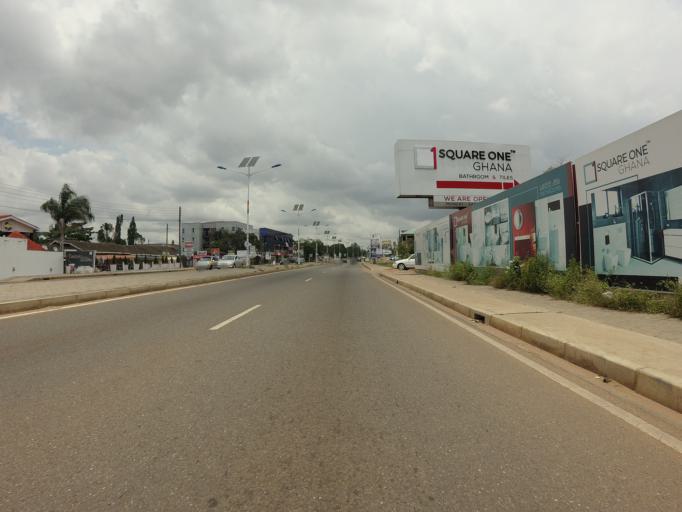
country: GH
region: Greater Accra
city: Medina Estates
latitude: 5.6539
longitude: -0.1509
